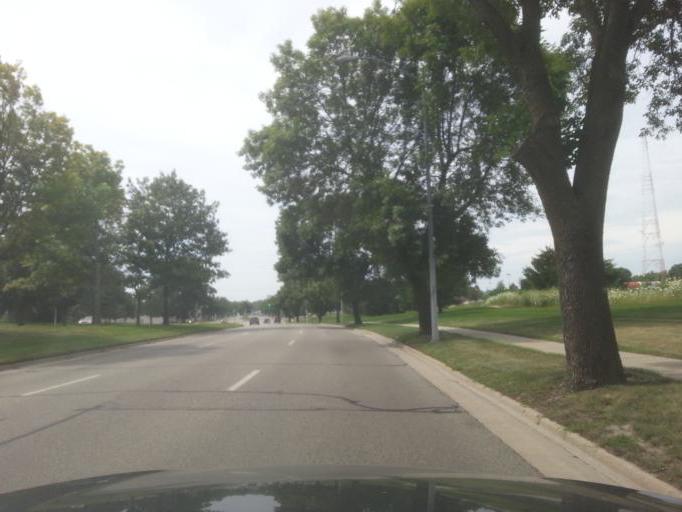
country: US
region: Wisconsin
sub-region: Dane County
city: Shorewood Hills
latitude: 43.0555
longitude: -89.4736
